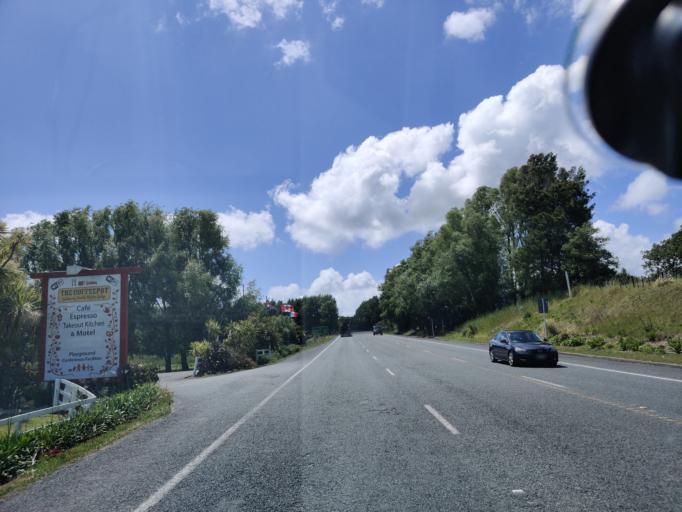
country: NZ
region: Auckland
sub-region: Auckland
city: Wellsford
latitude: -36.1584
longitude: 174.4417
